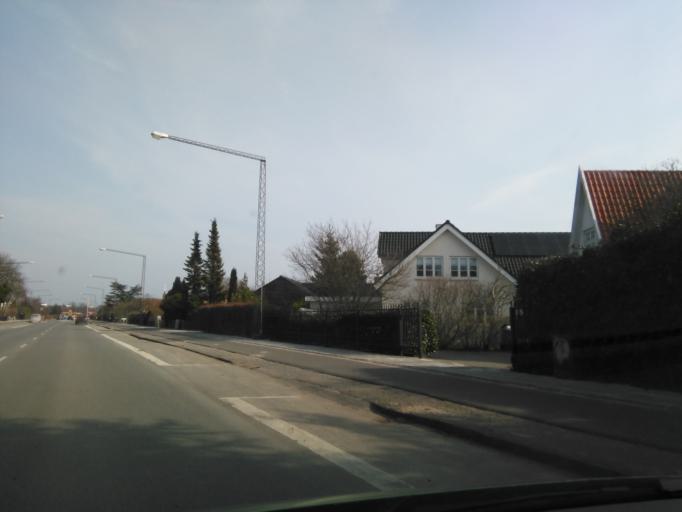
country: DK
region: Central Jutland
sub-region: Arhus Kommune
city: Lystrup
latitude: 56.1988
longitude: 10.2548
